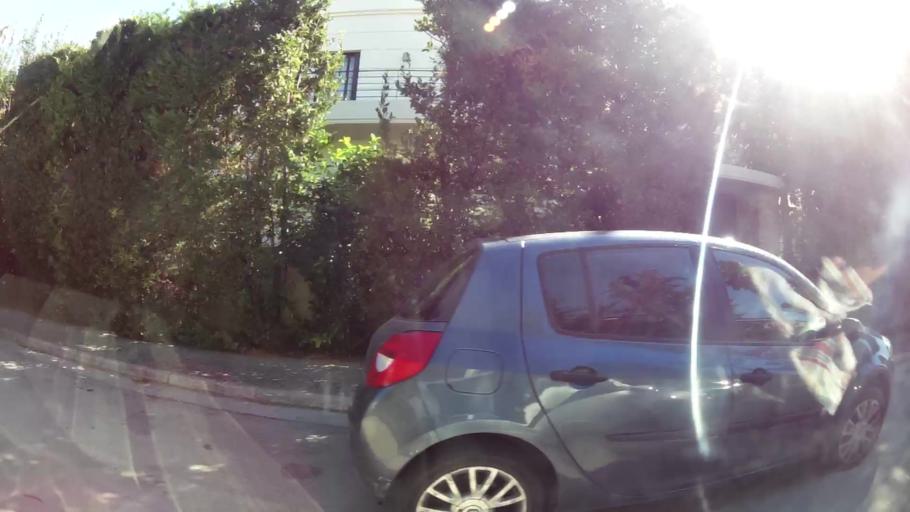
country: GR
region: Attica
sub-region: Nomarchia Athinas
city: Nea Erythraia
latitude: 38.0978
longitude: 23.8074
